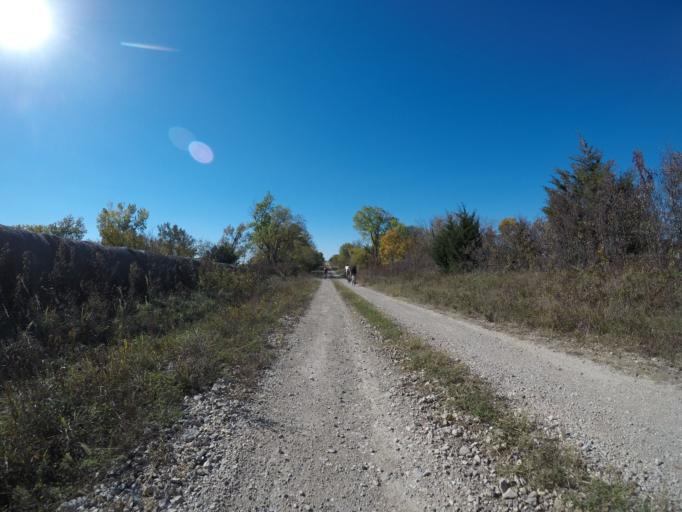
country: US
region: Kansas
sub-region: Wabaunsee County
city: Alma
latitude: 38.9711
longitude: -96.4668
